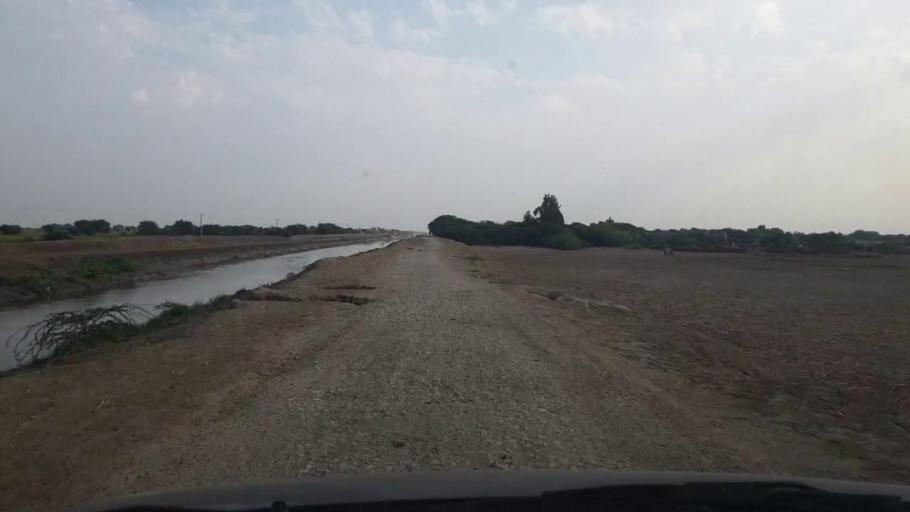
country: PK
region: Sindh
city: Badin
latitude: 24.5261
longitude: 68.6801
